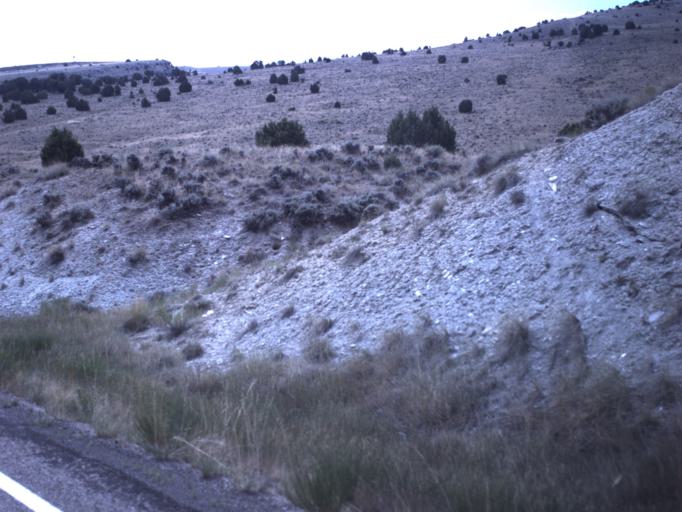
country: US
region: Utah
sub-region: Daggett County
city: Manila
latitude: 40.9171
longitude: -109.6914
